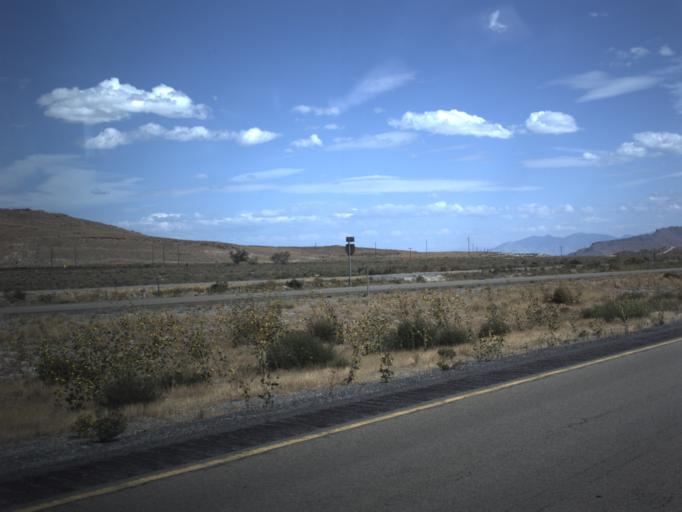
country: US
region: Utah
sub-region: Tooele County
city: Grantsville
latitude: 40.7678
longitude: -112.7909
